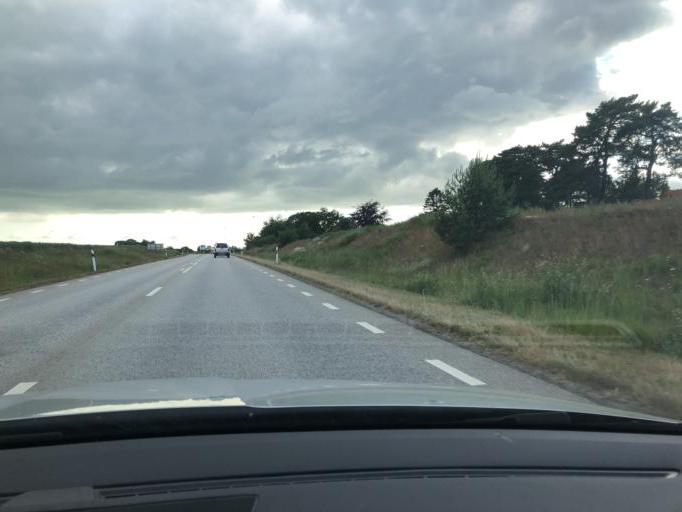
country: SE
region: Skane
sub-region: Simrishamns Kommun
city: Simrishamn
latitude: 55.5355
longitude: 14.2832
